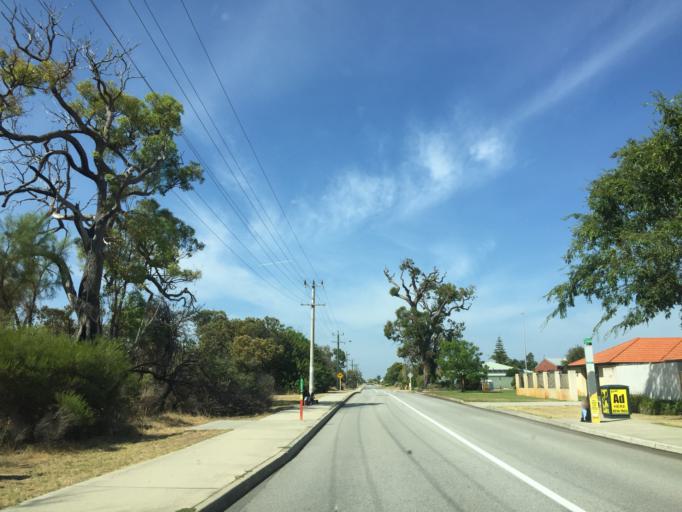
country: AU
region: Western Australia
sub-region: Gosnells
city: Thornlie
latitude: -32.0818
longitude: 115.9608
